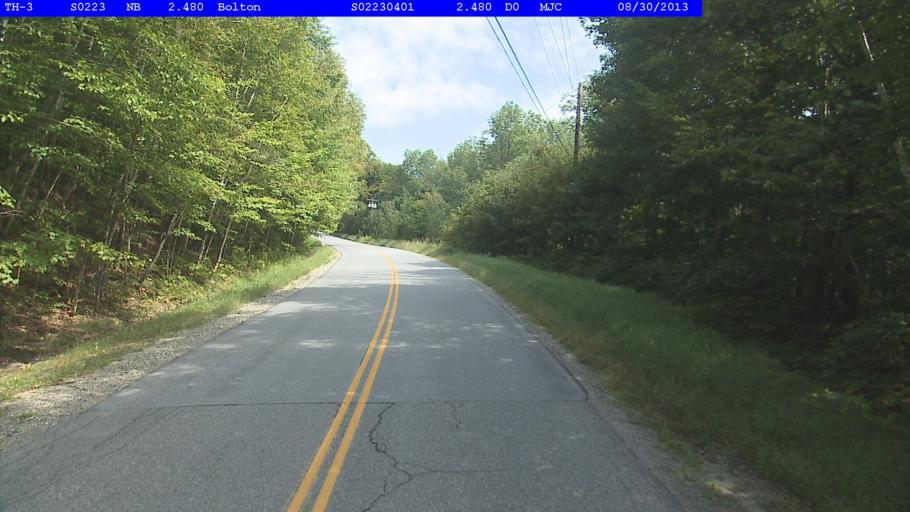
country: US
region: Vermont
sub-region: Washington County
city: Waterbury
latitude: 44.4039
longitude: -72.8741
